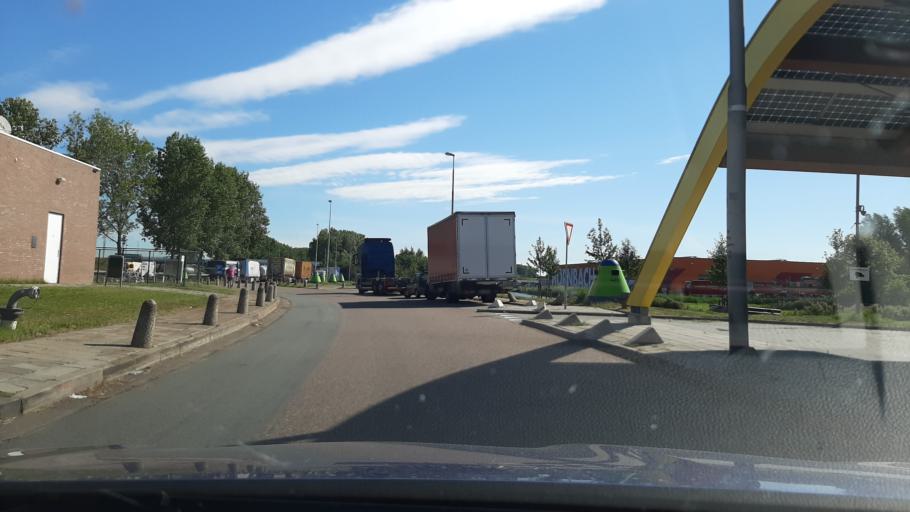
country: NL
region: South Holland
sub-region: Gemeente Capelle aan den IJssel
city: Capelle aan den IJssel
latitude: 51.9661
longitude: 4.5886
